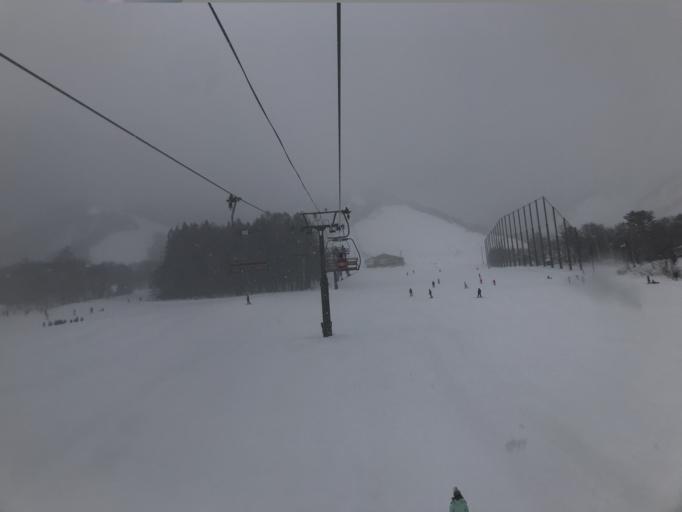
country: JP
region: Nagano
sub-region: Kitaazumi Gun
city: Hakuba
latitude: 36.7531
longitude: 137.8668
